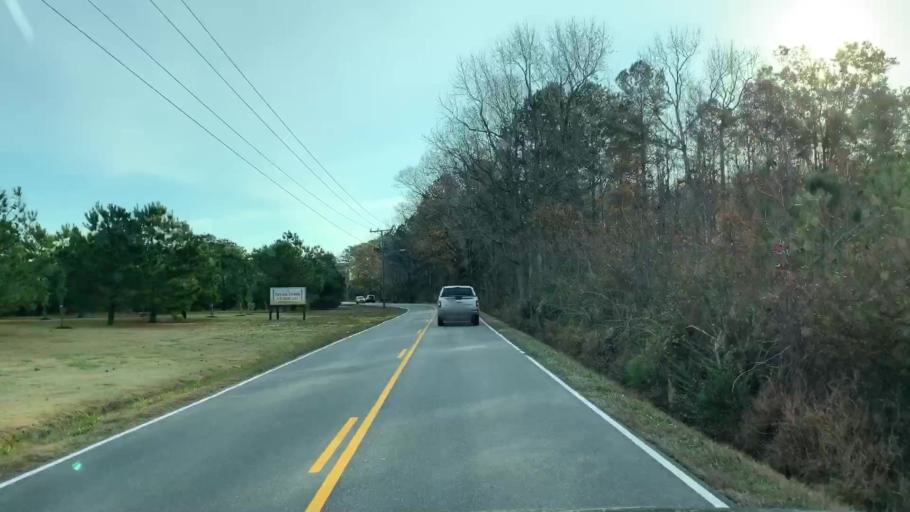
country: US
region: Virginia
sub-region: City of Virginia Beach
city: Virginia Beach
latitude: 36.7237
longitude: -76.0663
